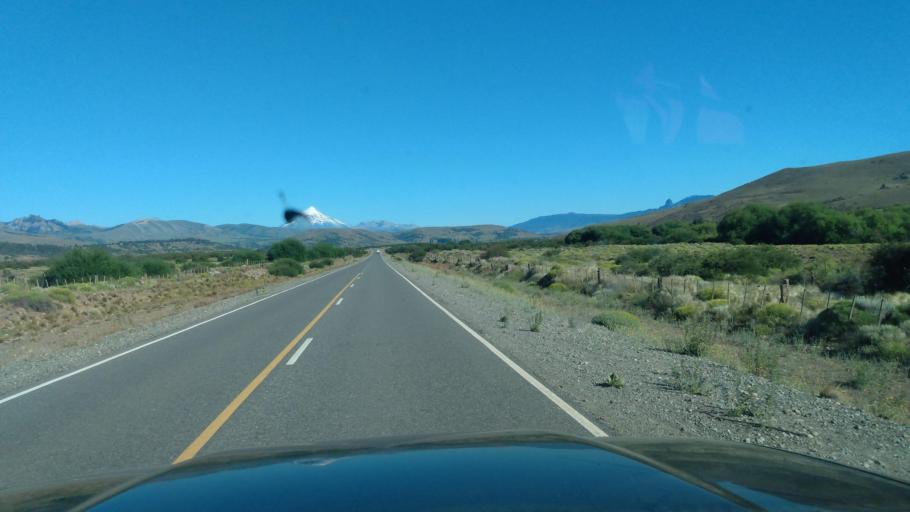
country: AR
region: Neuquen
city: Junin de los Andes
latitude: -39.8898
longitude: -71.1530
